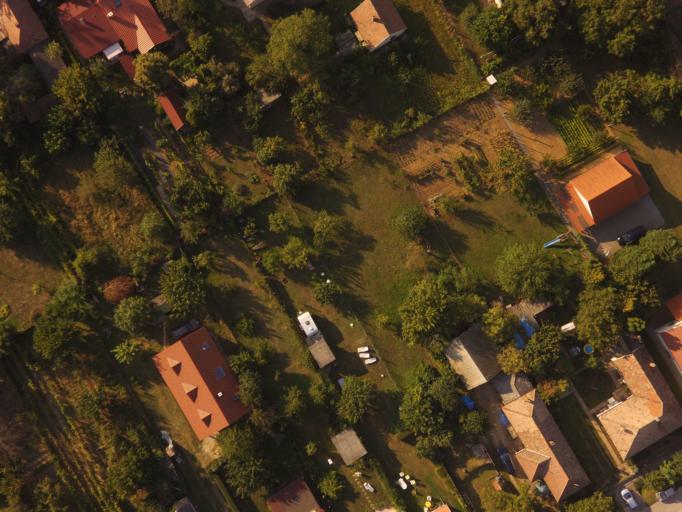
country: HU
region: Somogy
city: Balatonszarszo
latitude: 46.8105
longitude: 17.7849
